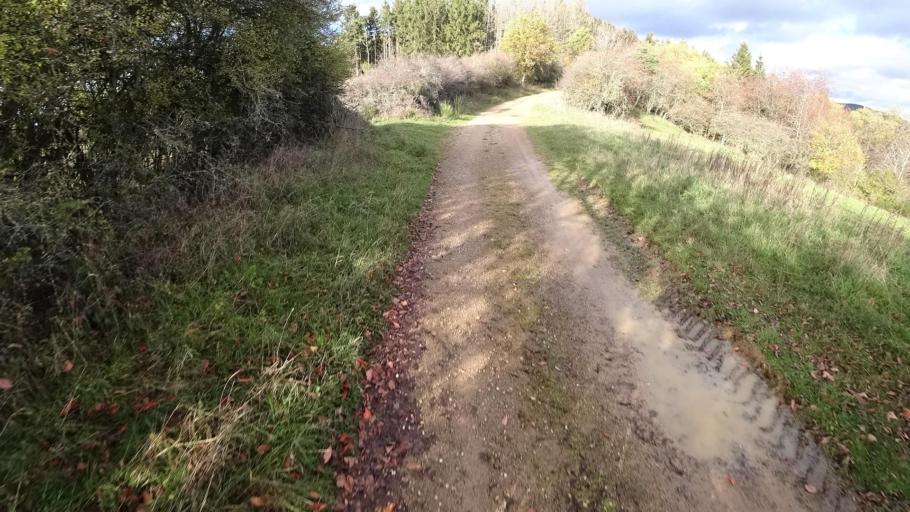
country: DE
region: Rheinland-Pfalz
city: Honningen
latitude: 50.4660
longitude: 6.9400
